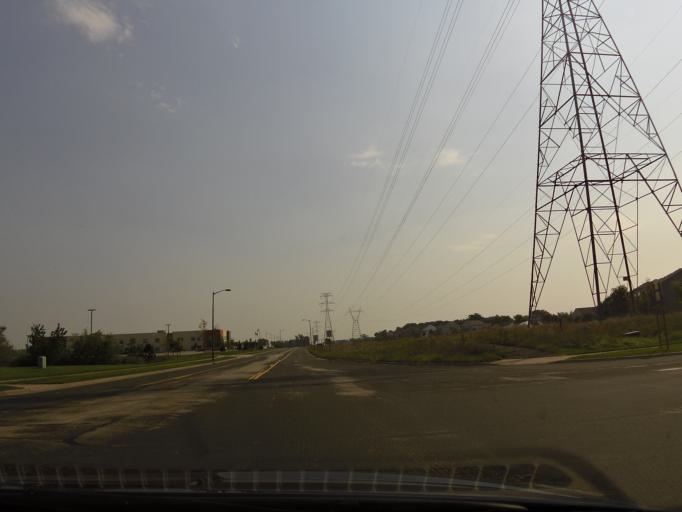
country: US
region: Minnesota
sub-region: Scott County
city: Shakopee
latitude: 44.7809
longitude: -93.4602
